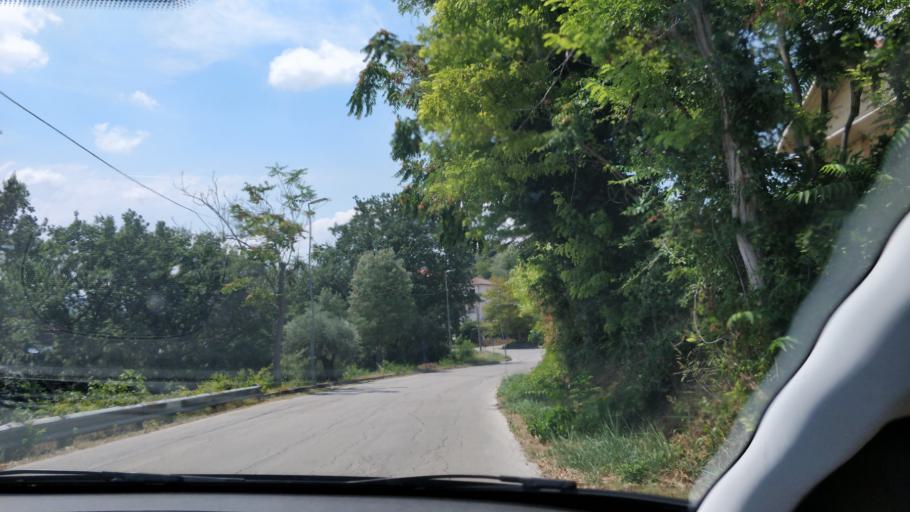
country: IT
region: Abruzzo
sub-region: Provincia di Chieti
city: Sambuceto
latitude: 42.4048
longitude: 14.1984
